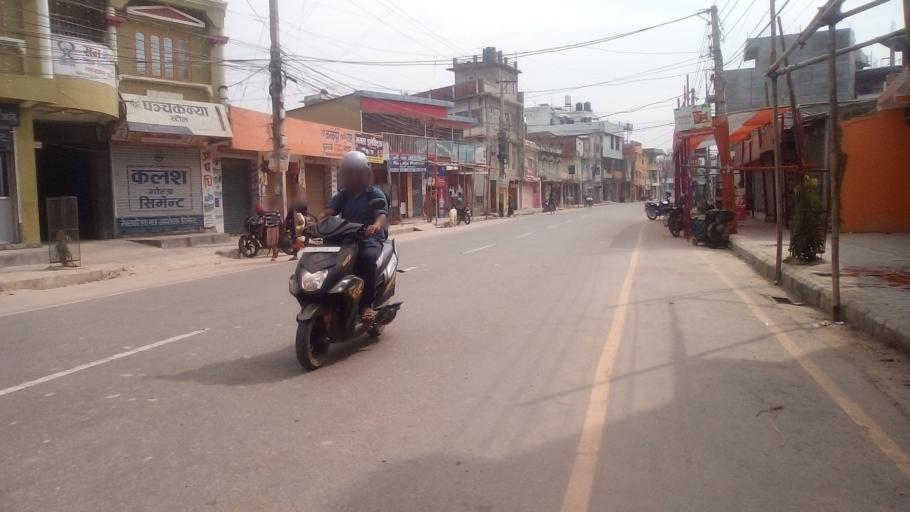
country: NP
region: Central Region
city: Janakpur
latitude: 26.7312
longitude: 85.9334
